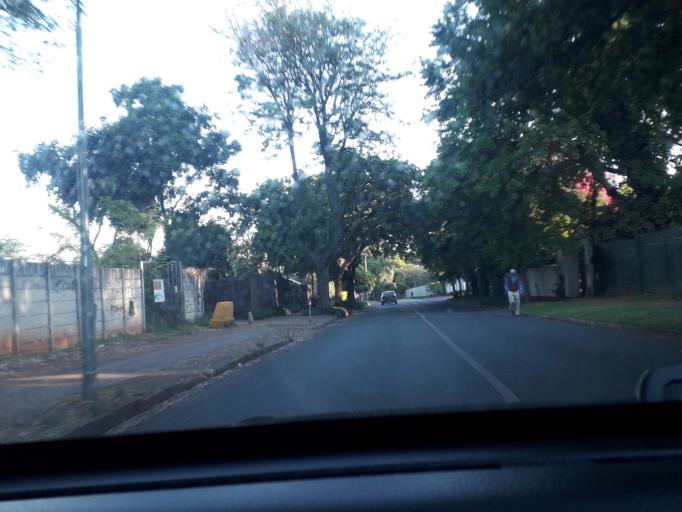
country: ZA
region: Gauteng
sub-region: City of Johannesburg Metropolitan Municipality
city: Johannesburg
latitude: -26.1622
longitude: 28.0501
